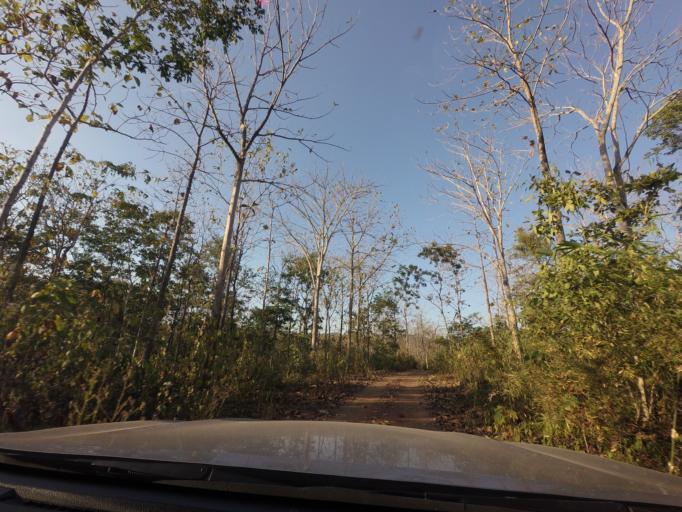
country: TH
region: Lampang
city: Mae Mo
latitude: 18.4162
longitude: 99.7385
